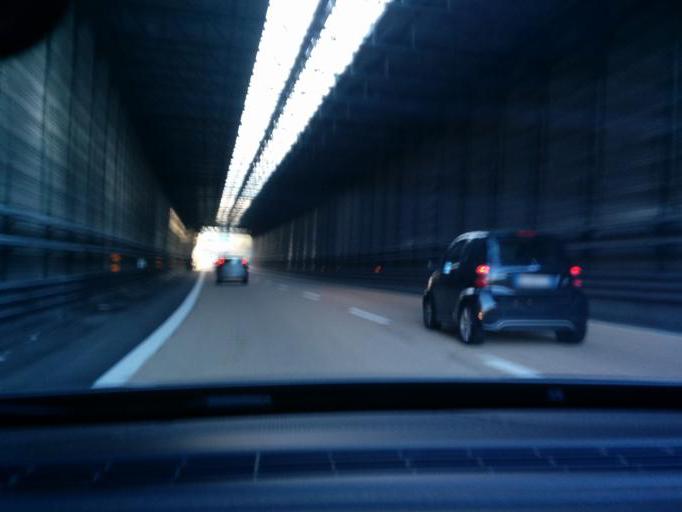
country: IT
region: Liguria
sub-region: Provincia di Genova
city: Genoa
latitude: 44.4547
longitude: 8.8990
